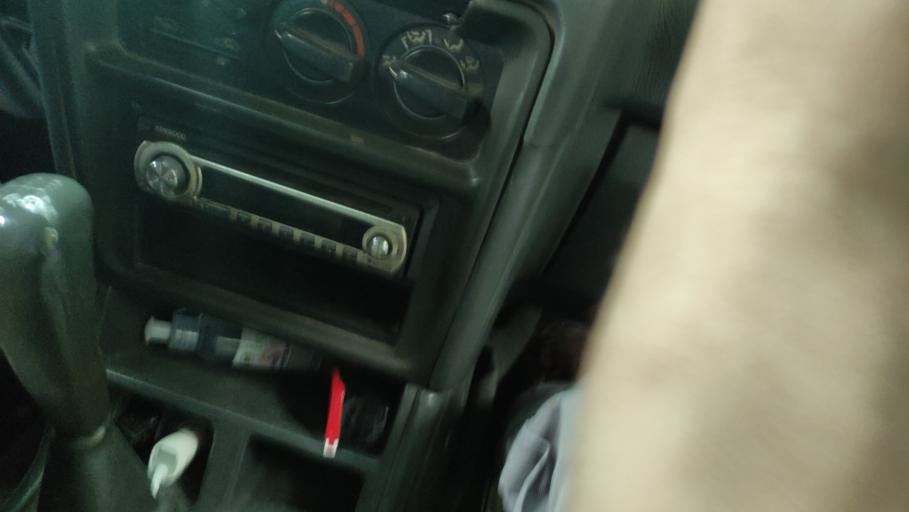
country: CO
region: Valle del Cauca
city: Cali
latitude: 3.4502
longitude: -76.6626
